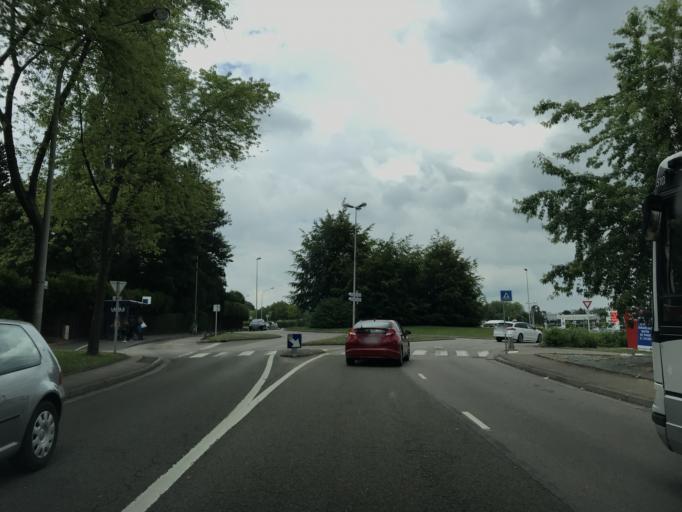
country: FR
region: Haute-Normandie
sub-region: Departement de la Seine-Maritime
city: Mont-Saint-Aignan
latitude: 49.4706
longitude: 1.0914
